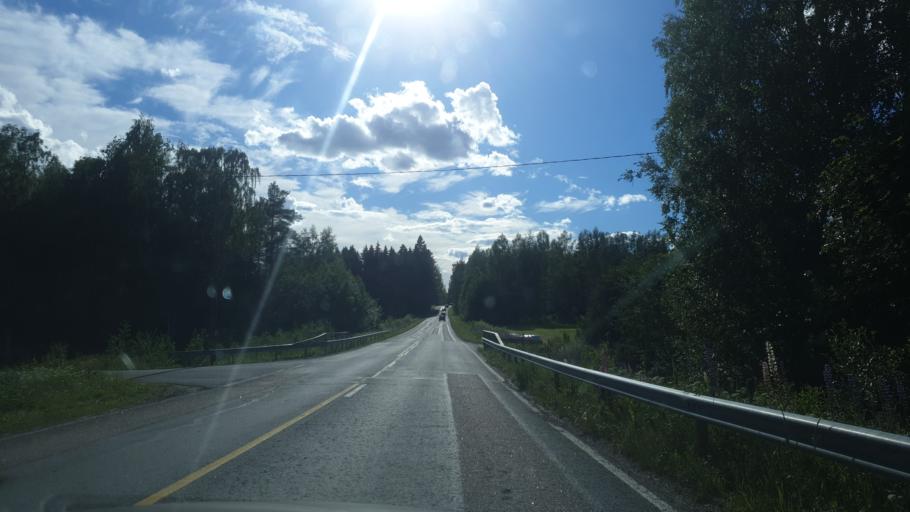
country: FI
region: Southern Savonia
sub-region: Mikkeli
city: Pertunmaa
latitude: 61.5234
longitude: 26.5213
